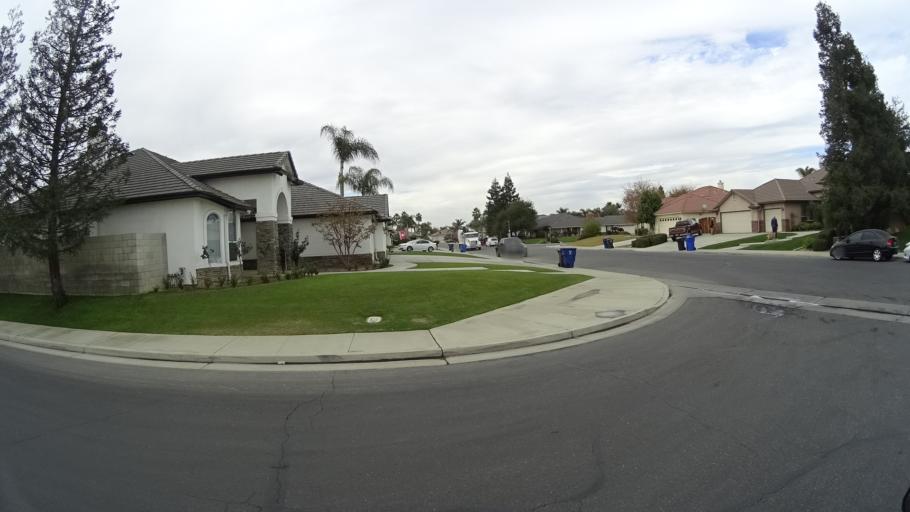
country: US
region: California
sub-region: Kern County
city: Rosedale
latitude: 35.4163
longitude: -119.1295
